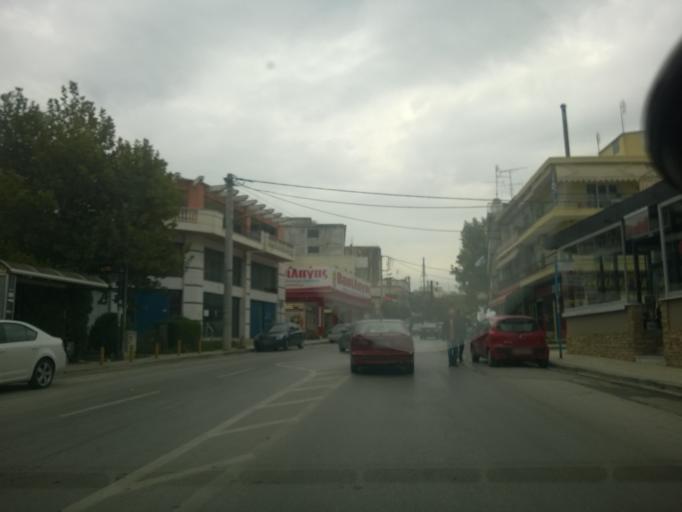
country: GR
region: Central Macedonia
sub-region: Nomos Thessalonikis
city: Stavroupoli
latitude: 40.6734
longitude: 22.9343
